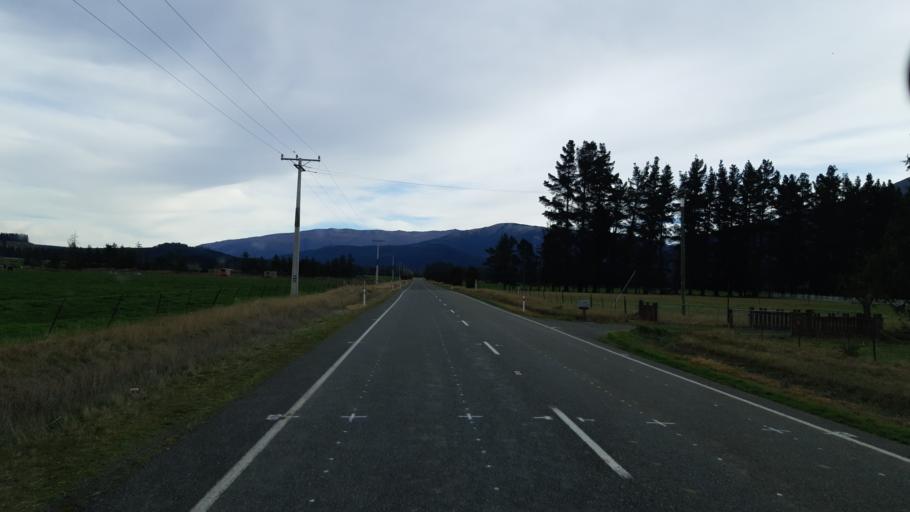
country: NZ
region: Tasman
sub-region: Tasman District
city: Brightwater
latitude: -41.6532
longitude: 173.2731
